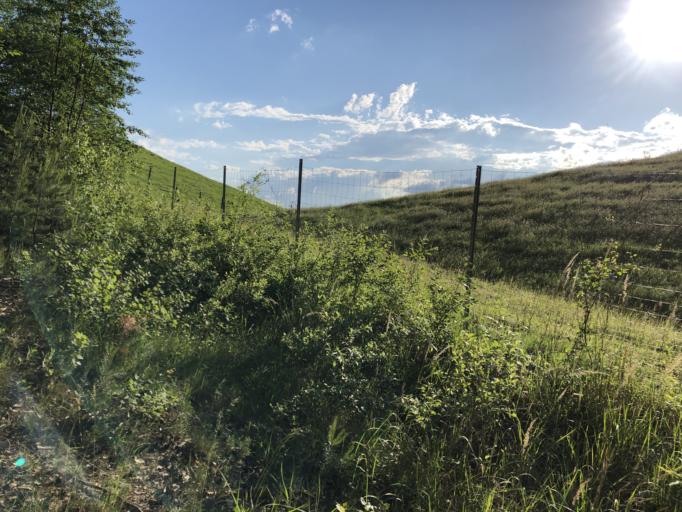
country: DE
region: Bavaria
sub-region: Upper Franconia
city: Memmelsdorf
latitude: 49.9157
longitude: 10.9514
